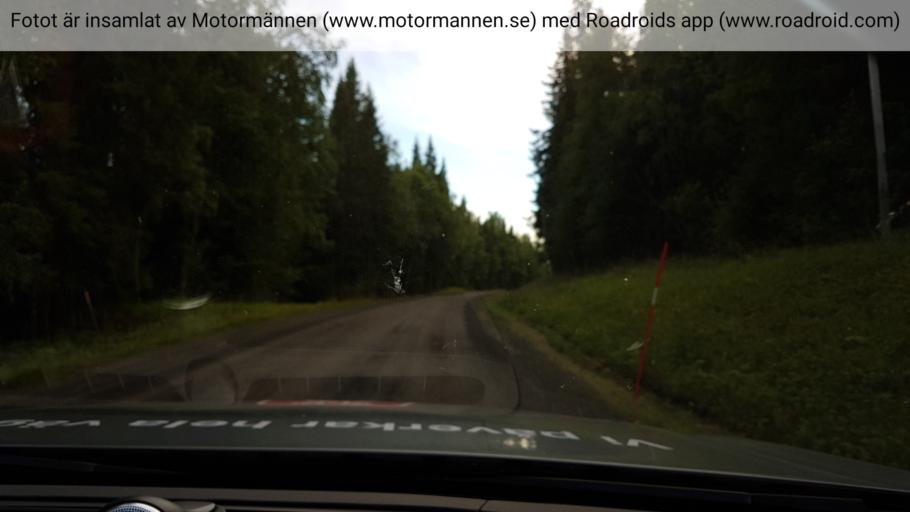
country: SE
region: Jaemtland
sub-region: Stroemsunds Kommun
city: Stroemsund
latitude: 64.0983
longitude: 15.8254
